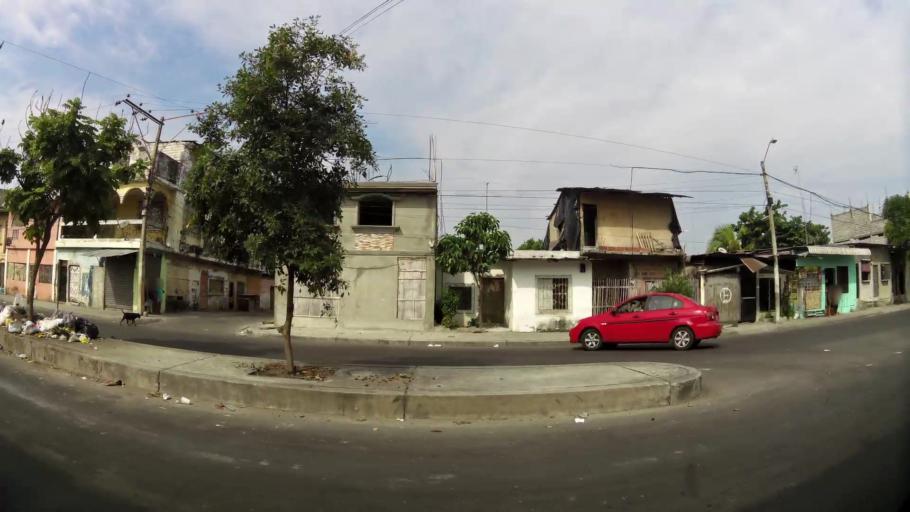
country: EC
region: Guayas
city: Guayaquil
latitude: -2.2595
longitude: -79.9032
